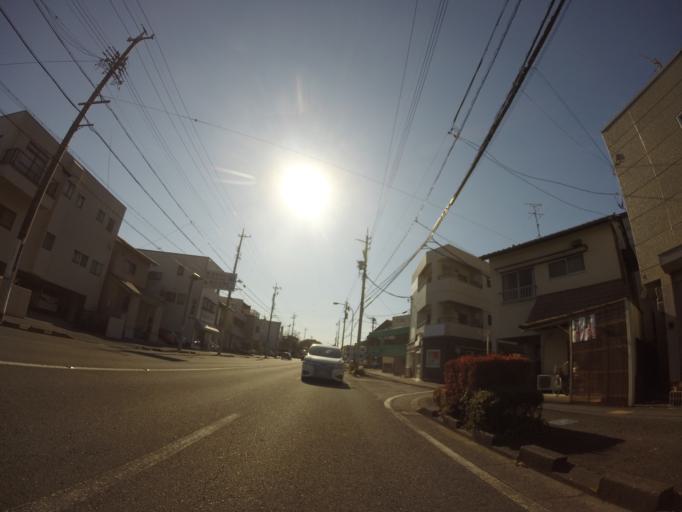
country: JP
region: Shizuoka
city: Shizuoka-shi
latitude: 34.9918
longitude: 138.3777
